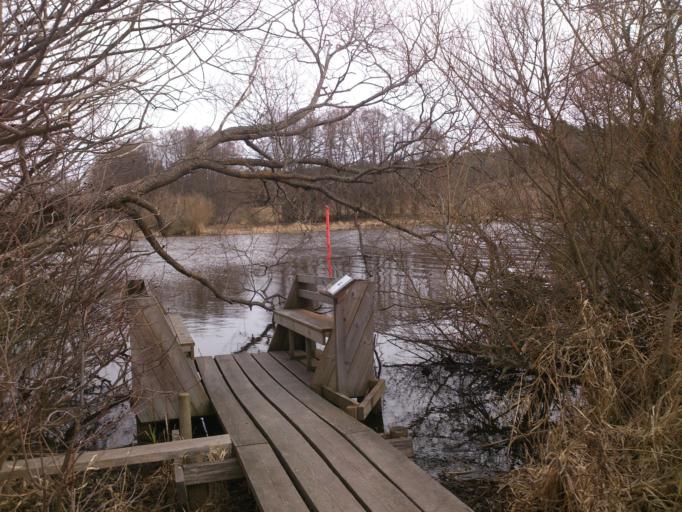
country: SE
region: Uppsala
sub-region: Uppsala Kommun
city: Saevja
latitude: 59.8044
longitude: 17.6667
